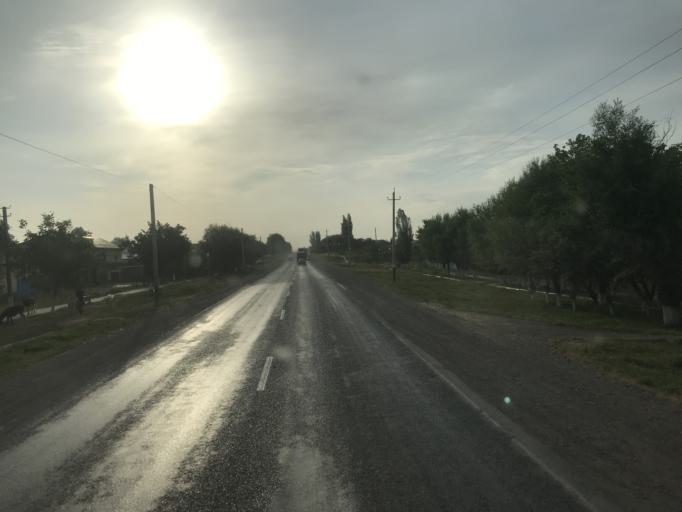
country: UZ
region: Toshkent
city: Salor
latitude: 41.4937
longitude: 69.3103
